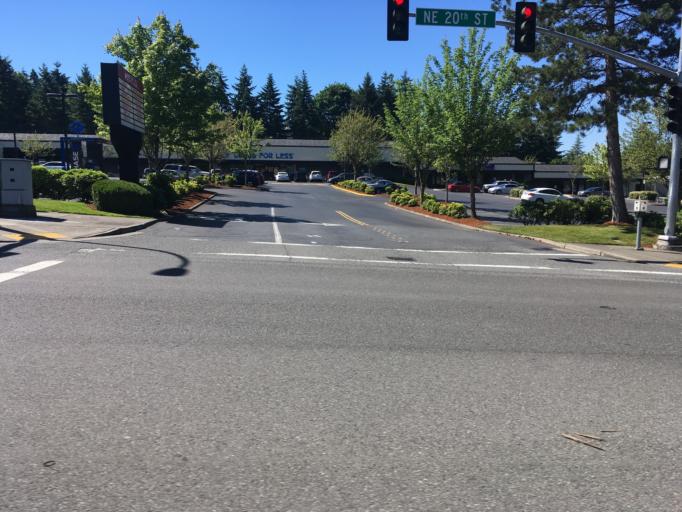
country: US
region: Washington
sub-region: King County
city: Redmond
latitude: 47.6280
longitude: -122.1494
